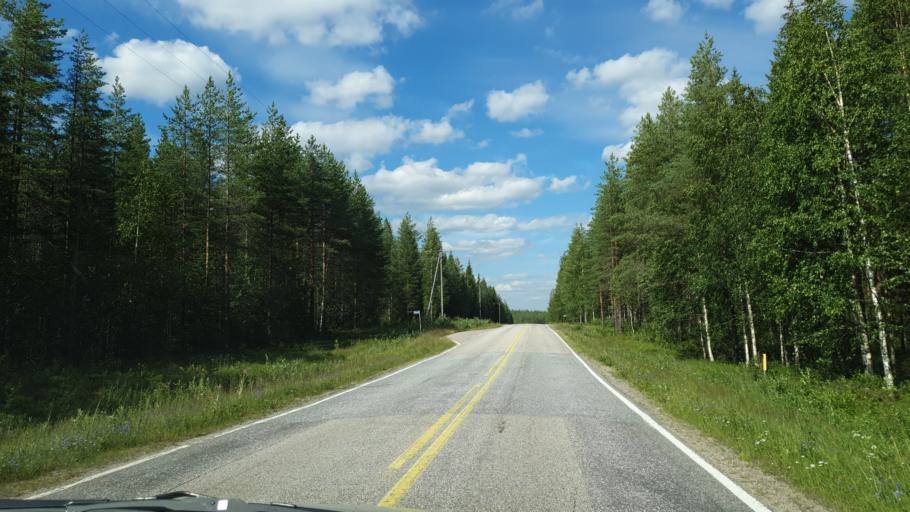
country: FI
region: Kainuu
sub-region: Kajaani
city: Sotkamo
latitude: 64.1907
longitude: 28.8953
